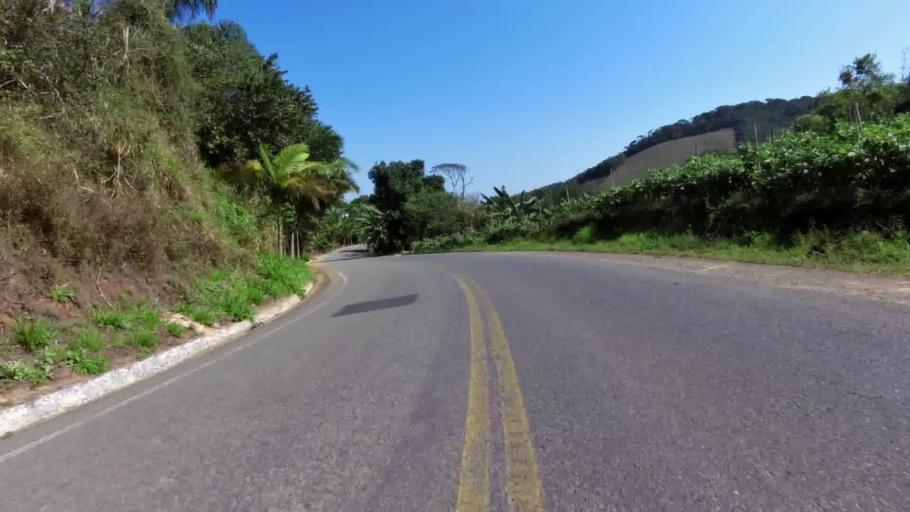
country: BR
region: Espirito Santo
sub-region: Alfredo Chaves
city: Alfredo Chaves
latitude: -20.5487
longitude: -40.7905
